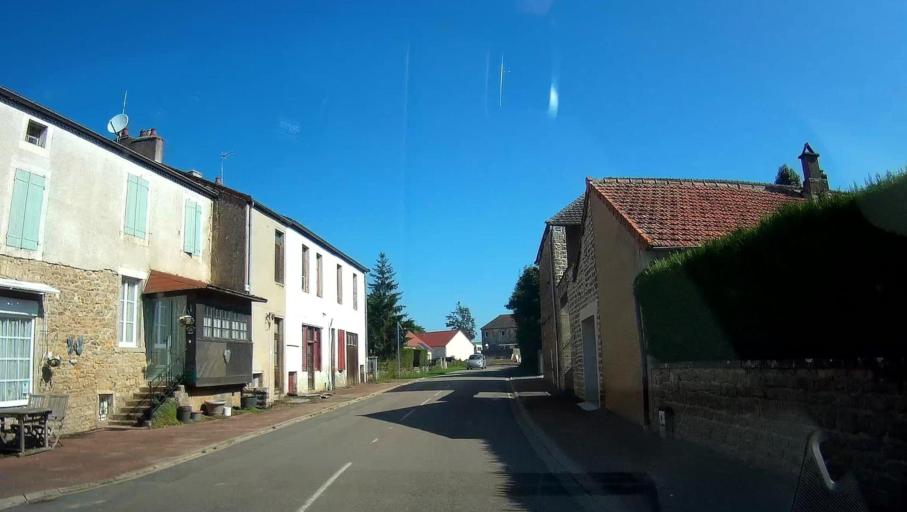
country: FR
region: Bourgogne
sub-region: Departement de Saone-et-Loire
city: Couches
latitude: 46.9100
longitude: 4.5962
